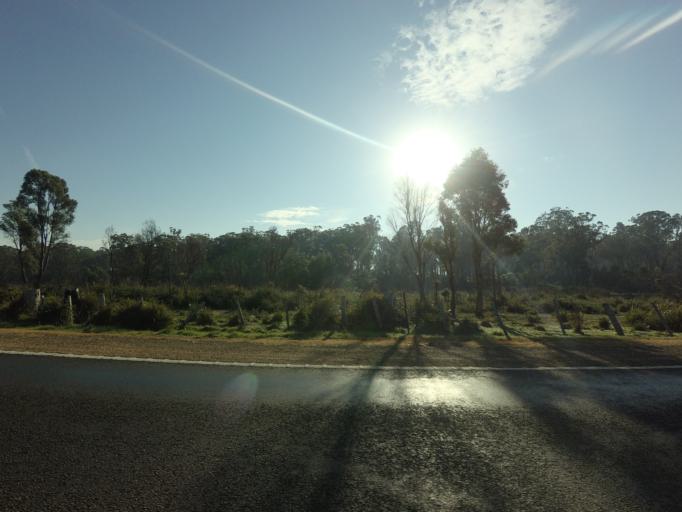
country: AU
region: Tasmania
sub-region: Launceston
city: Summerhill
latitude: -41.5299
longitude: 147.0372
